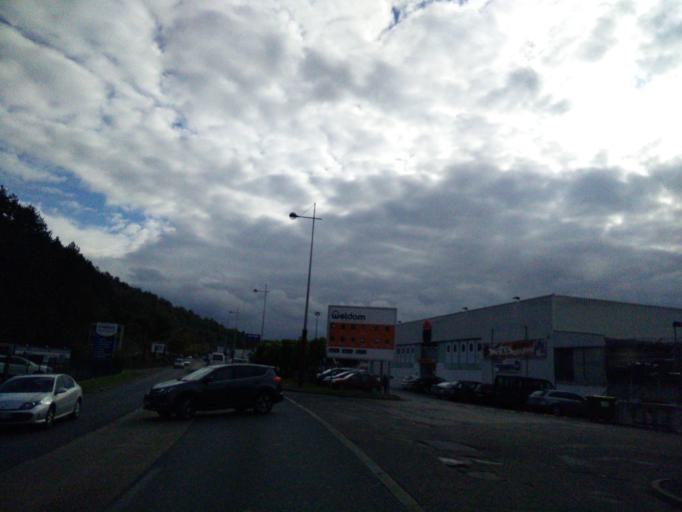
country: FR
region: Midi-Pyrenees
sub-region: Departement du Lot
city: Cahors
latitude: 44.4224
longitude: 1.4393
